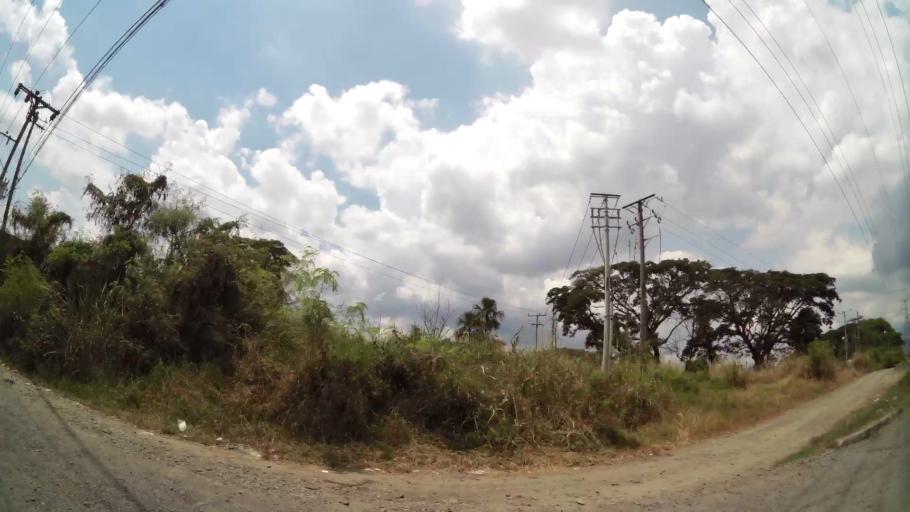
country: CO
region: Valle del Cauca
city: Cali
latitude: 3.4531
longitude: -76.4705
